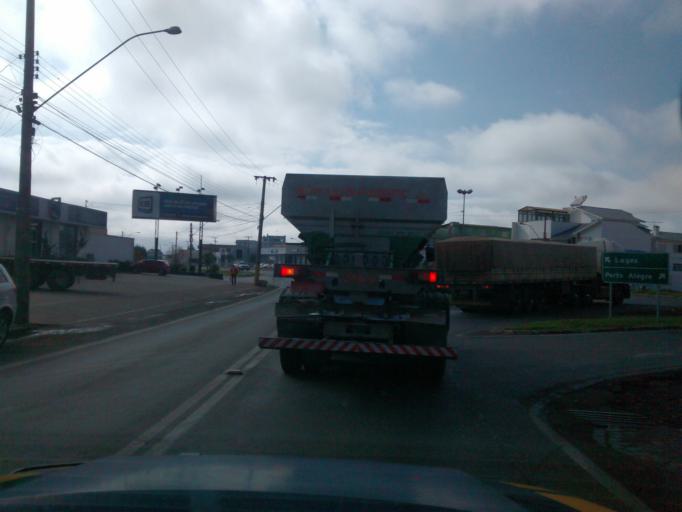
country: BR
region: Rio Grande do Sul
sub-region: Vacaria
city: Vacaria
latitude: -28.5091
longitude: -50.9297
